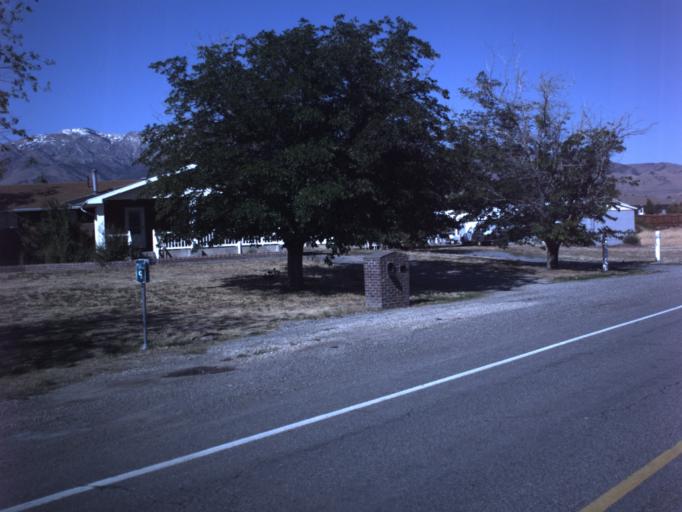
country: US
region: Utah
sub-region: Tooele County
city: Grantsville
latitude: 40.6031
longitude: -112.4855
